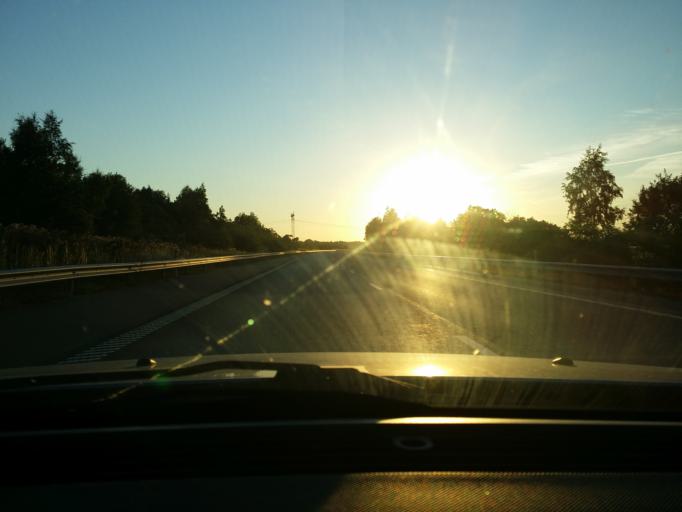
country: SE
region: Uppsala
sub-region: Habo Kommun
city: Balsta
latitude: 59.5933
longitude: 17.4736
